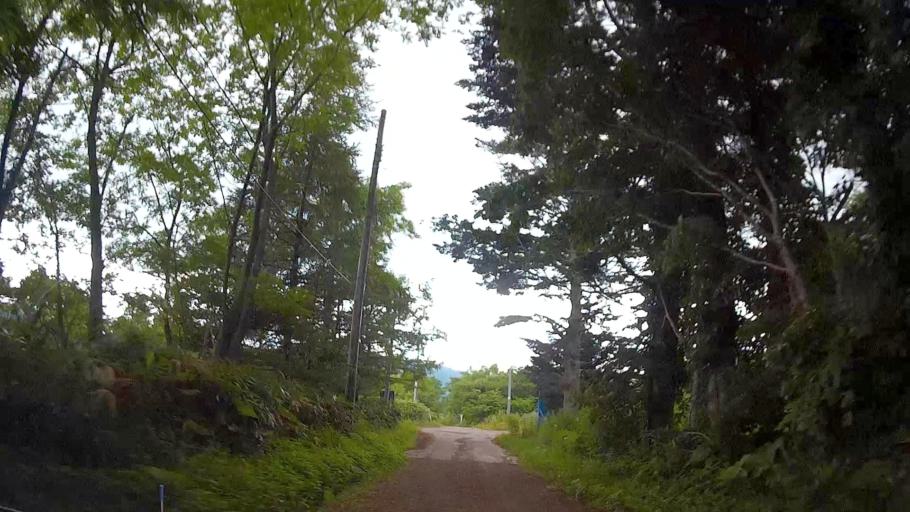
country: JP
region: Hokkaido
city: Nanae
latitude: 42.1279
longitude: 140.4120
